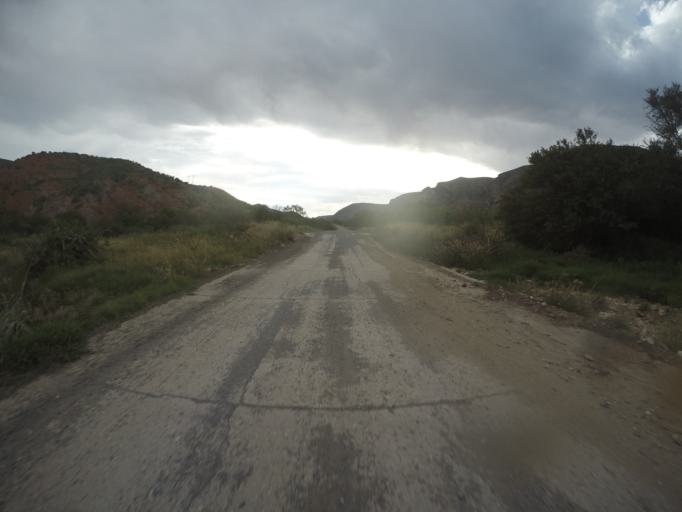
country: ZA
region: Eastern Cape
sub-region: Cacadu District Municipality
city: Willowmore
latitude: -33.5217
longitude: 23.8385
